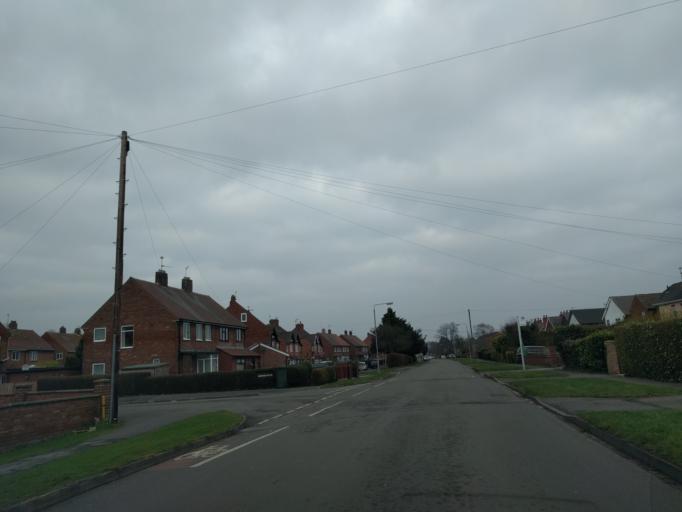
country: GB
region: England
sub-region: Nottinghamshire
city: Newark on Trent
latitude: 53.0882
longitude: -0.7985
